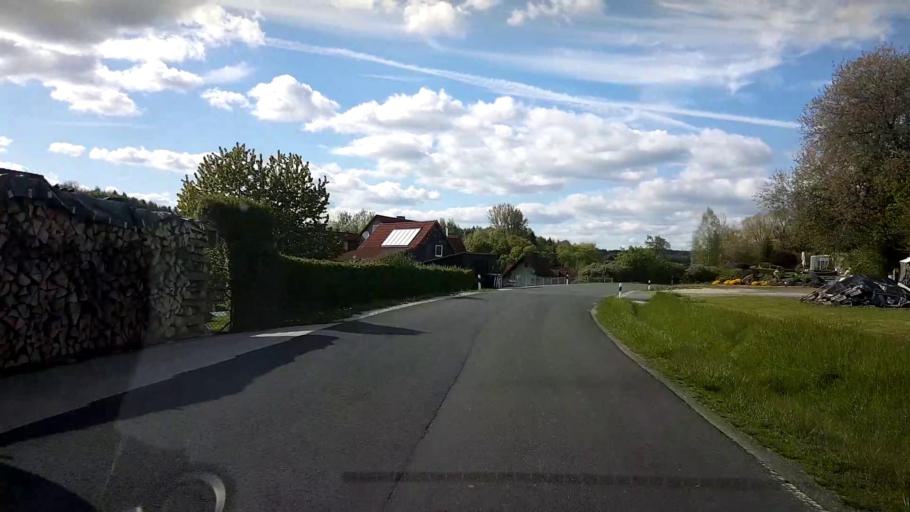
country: DE
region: Bavaria
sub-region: Upper Franconia
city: Hollfeld
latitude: 49.9425
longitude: 11.2832
